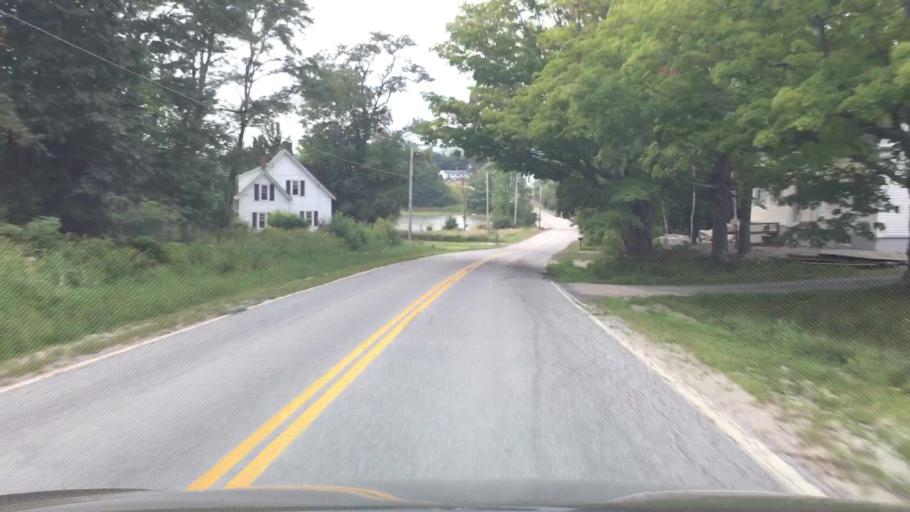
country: US
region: Maine
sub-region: Hancock County
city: Penobscot
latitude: 44.4613
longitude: -68.7066
